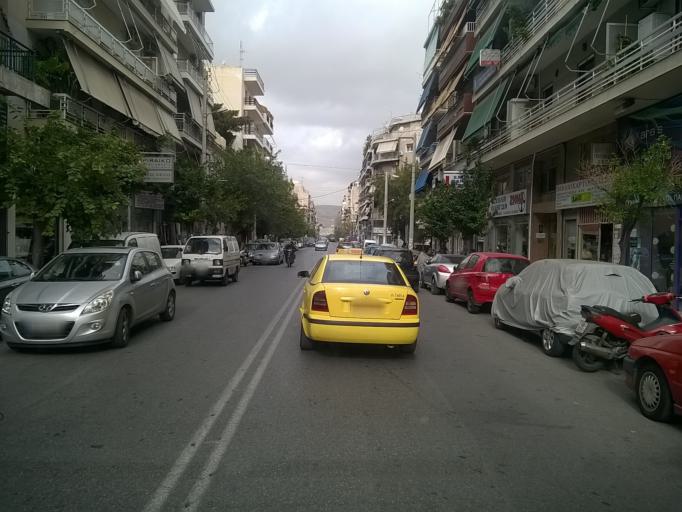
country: GR
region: Attica
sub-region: Nomos Attikis
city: Piraeus
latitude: 37.9334
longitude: 23.6420
